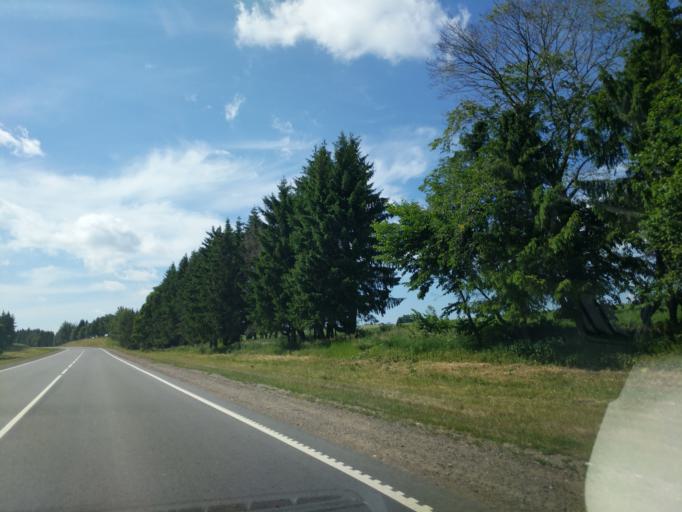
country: BY
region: Minsk
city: Syomkava
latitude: 54.1141
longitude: 27.4388
